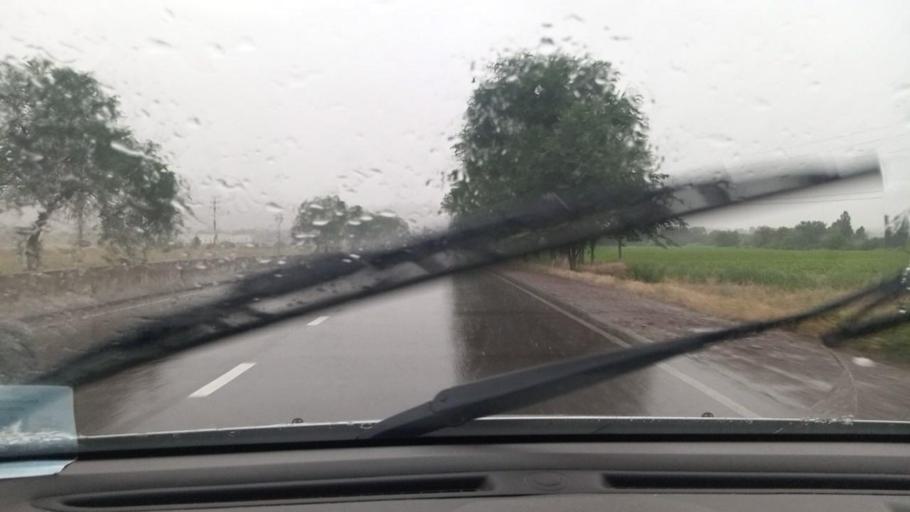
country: UZ
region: Toshkent
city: Ohangaron
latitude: 40.9197
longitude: 69.8359
